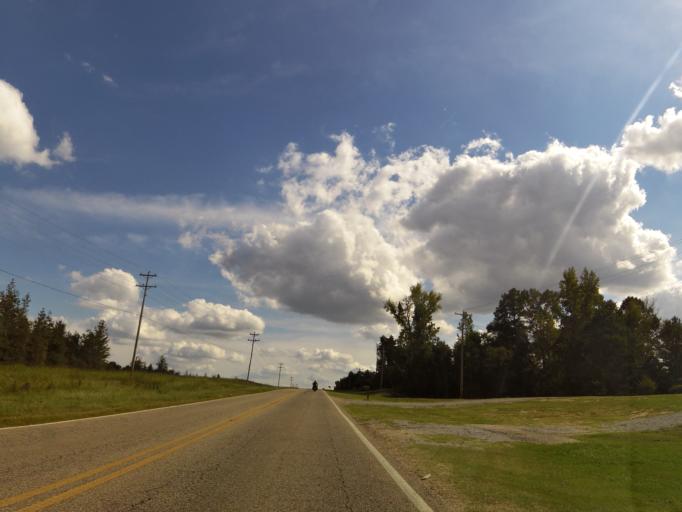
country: US
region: Alabama
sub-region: Dallas County
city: Selmont-West Selmont
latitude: 32.3217
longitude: -86.9907
